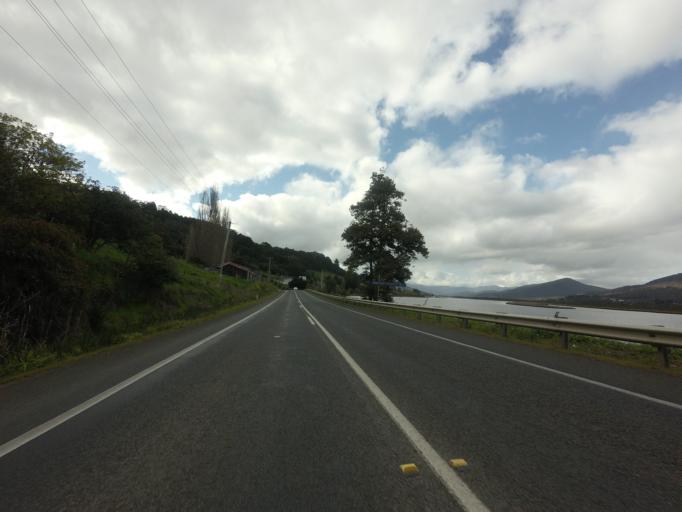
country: AU
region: Tasmania
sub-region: Huon Valley
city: Franklin
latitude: -43.1082
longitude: 147.0006
